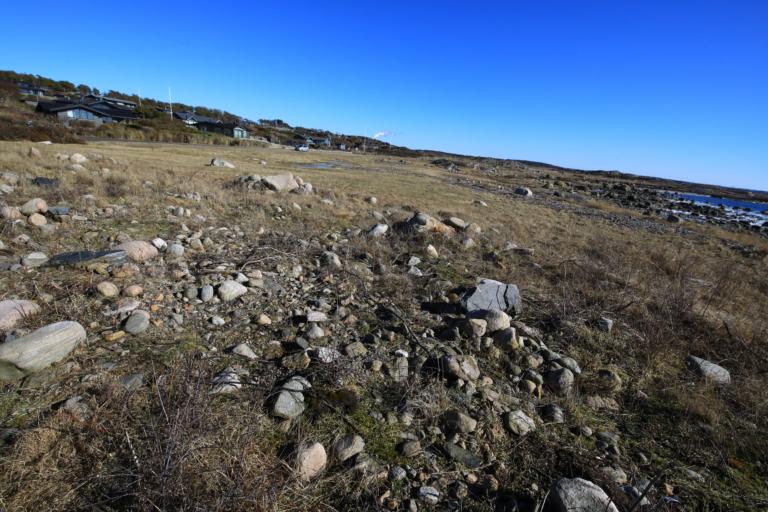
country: SE
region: Halland
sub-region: Kungsbacka Kommun
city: Frillesas
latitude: 57.2295
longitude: 12.1066
